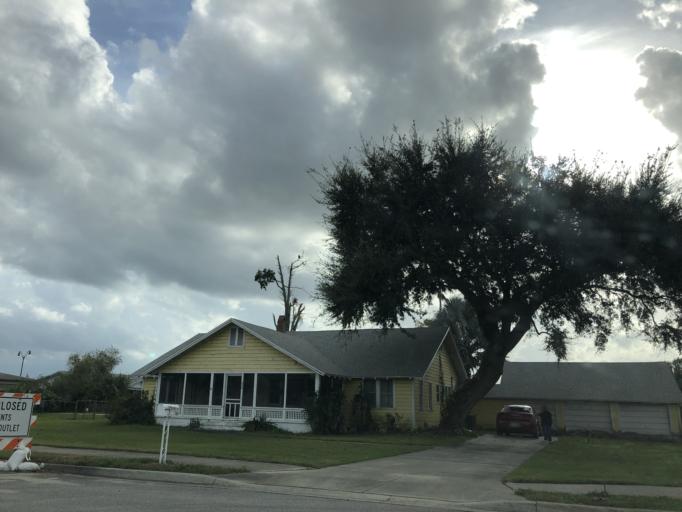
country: US
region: Florida
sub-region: Osceola County
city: Kissimmee
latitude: 28.2923
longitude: -81.4000
